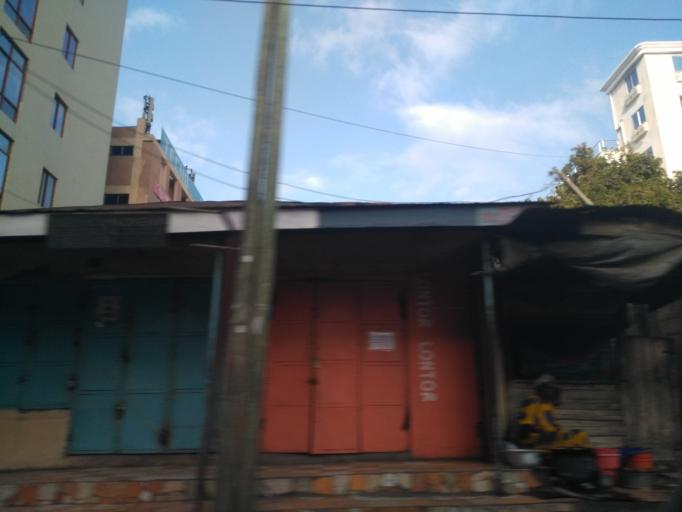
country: TZ
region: Arusha
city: Arusha
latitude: -3.3706
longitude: 36.6859
